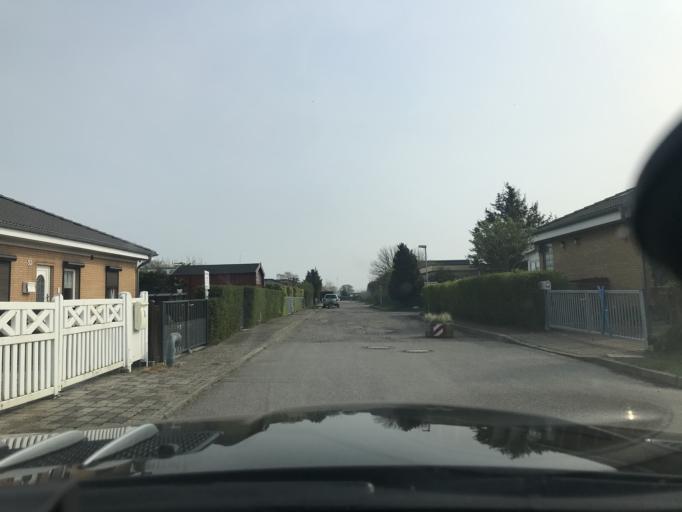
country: DE
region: Schleswig-Holstein
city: Burg auf Fehmarn
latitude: 54.4927
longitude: 11.2409
